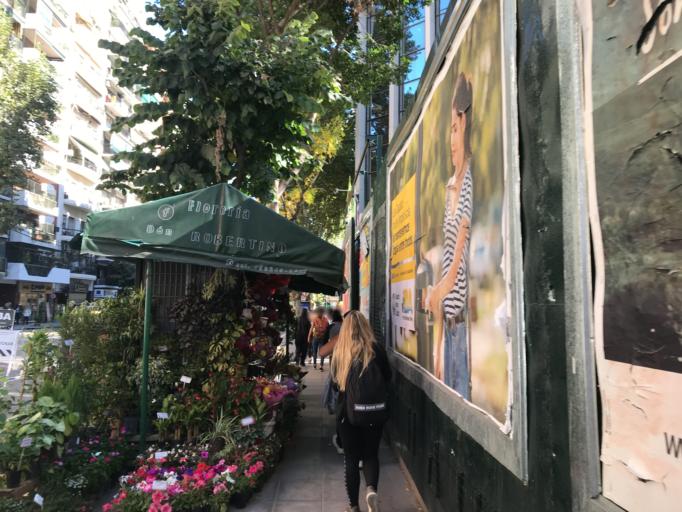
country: AR
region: Buenos Aires F.D.
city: Retiro
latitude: -34.5916
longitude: -58.4010
